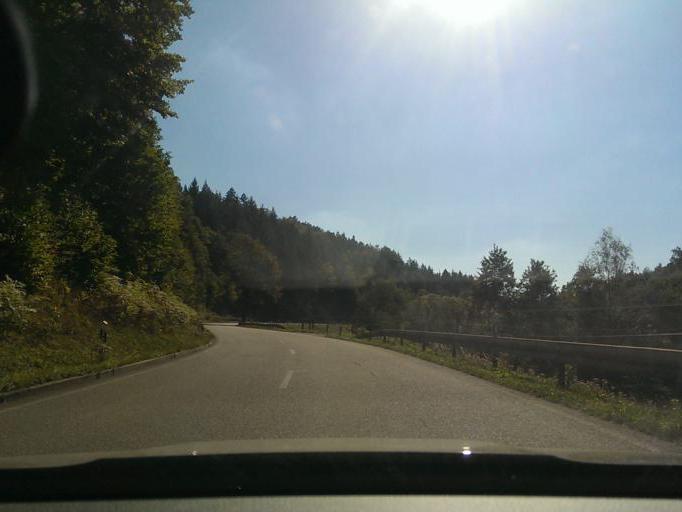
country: DE
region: Baden-Wuerttemberg
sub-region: Karlsruhe Region
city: Bad Herrenalb
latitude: 48.8434
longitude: 8.4392
